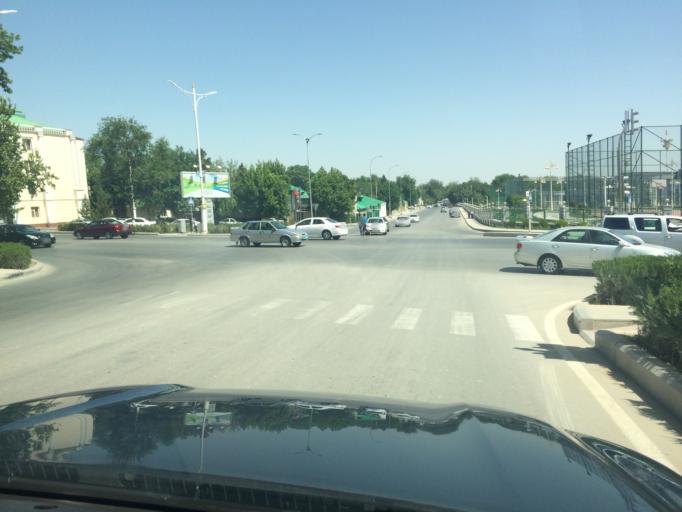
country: TM
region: Ahal
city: Ashgabat
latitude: 37.9430
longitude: 58.3603
